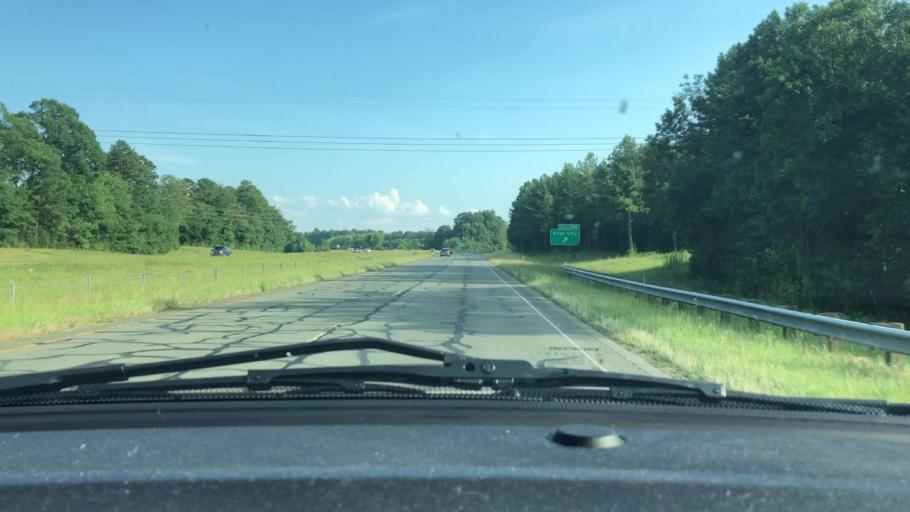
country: US
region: North Carolina
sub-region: Chatham County
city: Siler City
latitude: 35.6995
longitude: -79.4290
